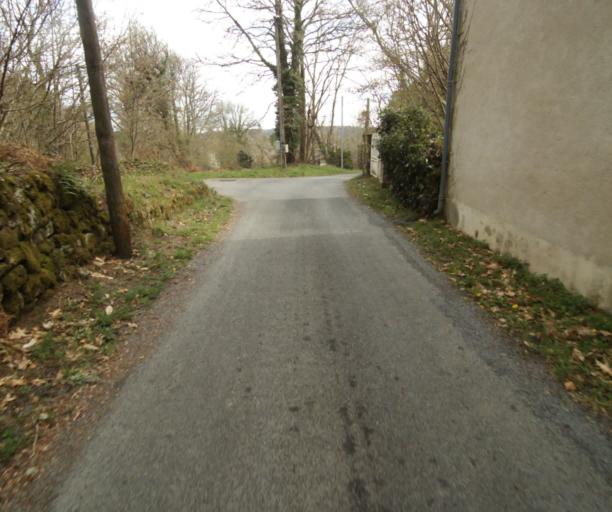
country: FR
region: Limousin
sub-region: Departement de la Correze
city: Argentat
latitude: 45.1998
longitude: 1.9577
